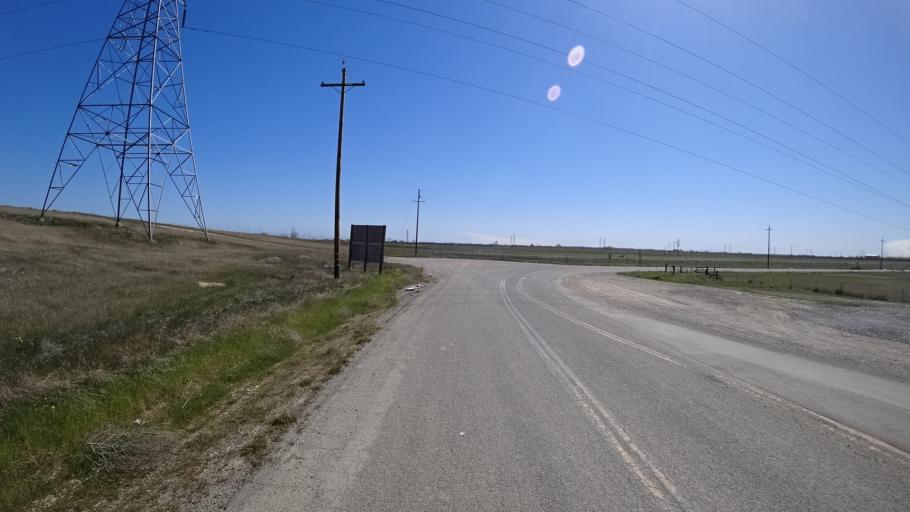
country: US
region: California
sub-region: Glenn County
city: Willows
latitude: 39.6310
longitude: -122.2737
